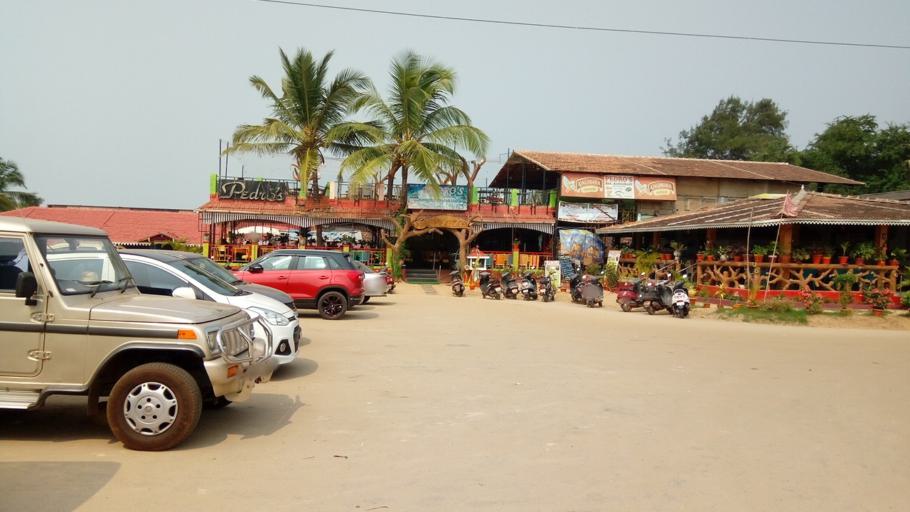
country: IN
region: Goa
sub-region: South Goa
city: Benaulim
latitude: 15.2569
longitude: 73.9197
